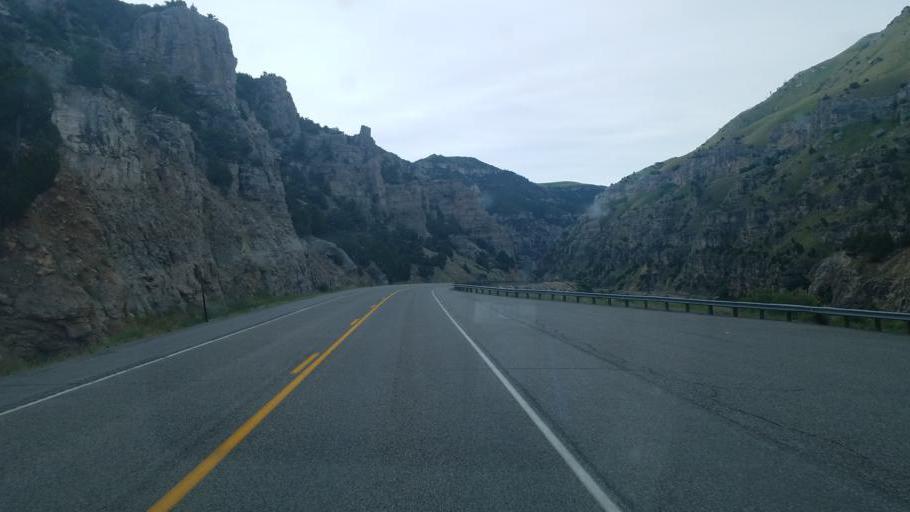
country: US
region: Wyoming
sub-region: Hot Springs County
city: Thermopolis
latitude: 43.5506
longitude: -108.1933
